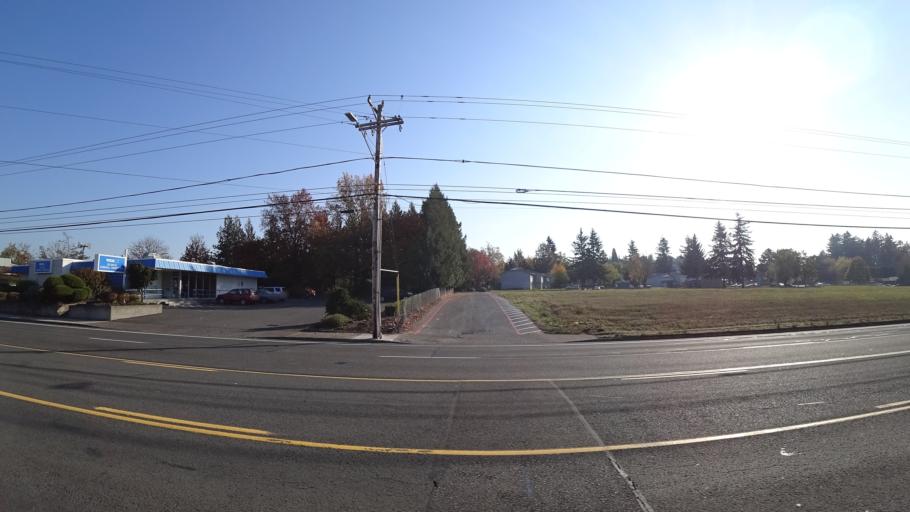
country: US
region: Oregon
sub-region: Multnomah County
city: Fairview
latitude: 45.5191
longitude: -122.4369
